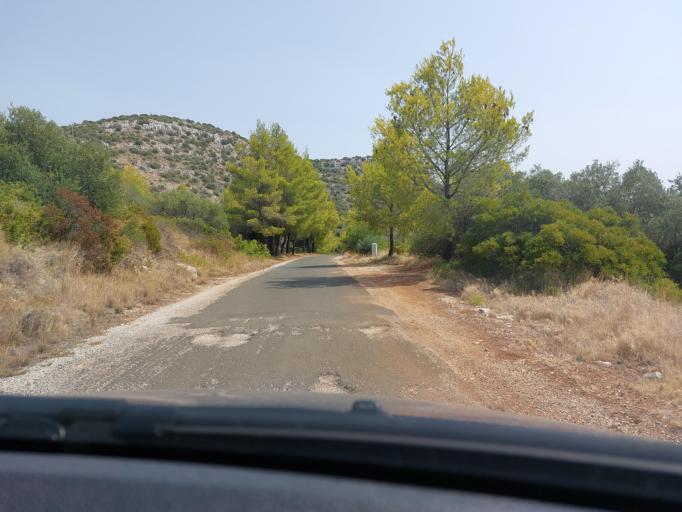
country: HR
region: Dubrovacko-Neretvanska
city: Smokvica
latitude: 42.7392
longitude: 16.8876
